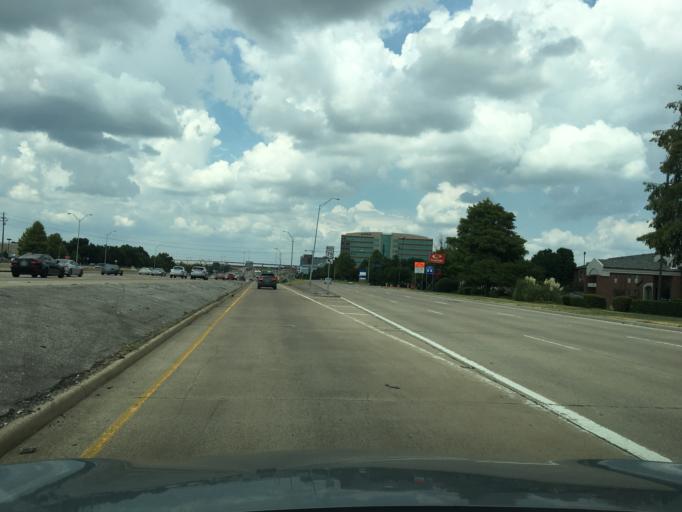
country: US
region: Texas
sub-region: Collin County
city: Plano
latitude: 32.9889
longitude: -96.7101
